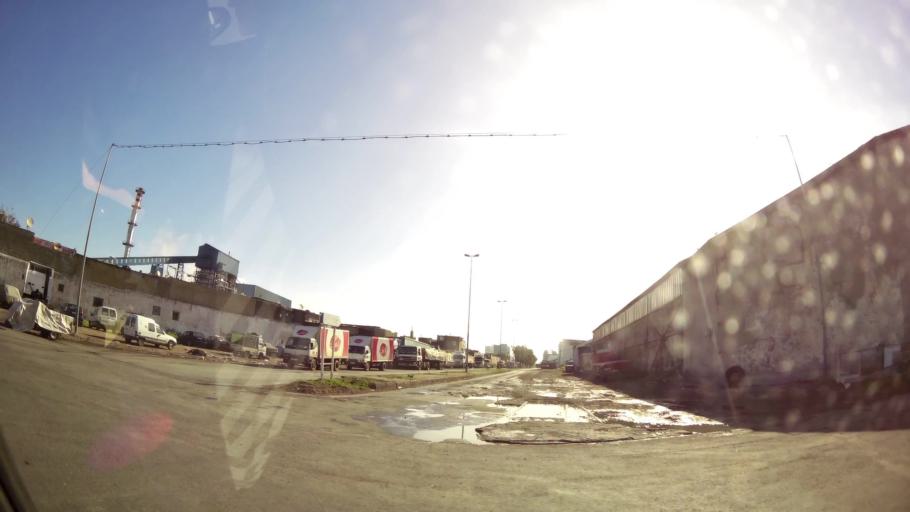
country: MA
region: Grand Casablanca
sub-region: Casablanca
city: Casablanca
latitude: 33.6009
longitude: -7.5731
